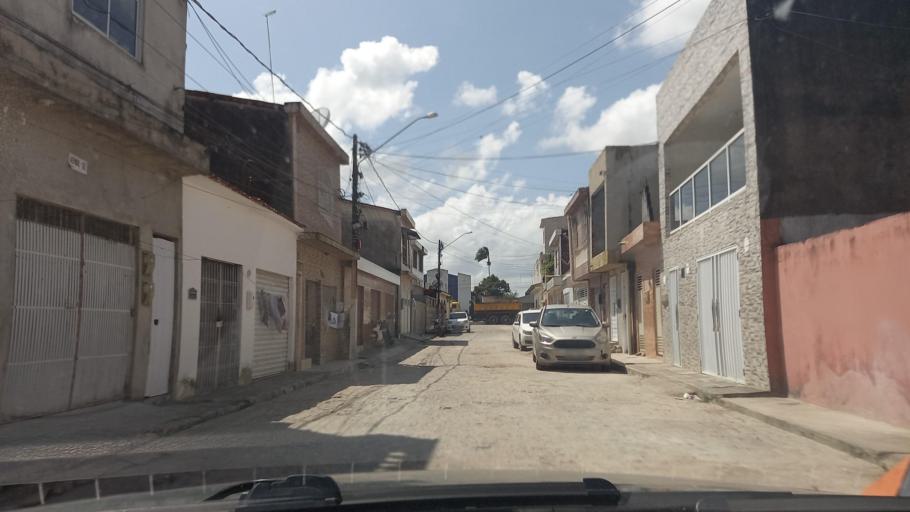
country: BR
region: Pernambuco
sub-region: Goiana
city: Goiana
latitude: -7.5642
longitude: -34.9942
